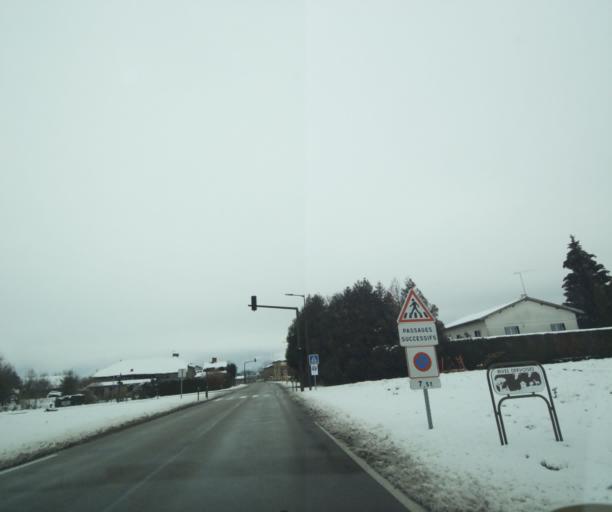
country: FR
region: Champagne-Ardenne
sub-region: Departement de la Haute-Marne
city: Montier-en-Der
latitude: 48.4324
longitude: 4.7136
